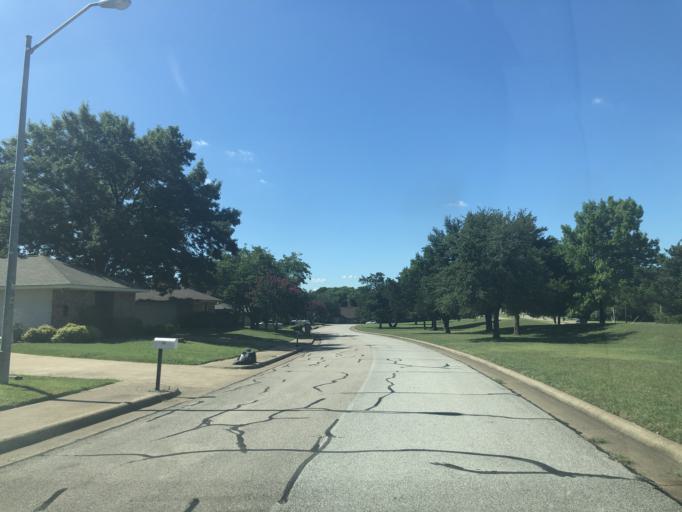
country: US
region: Texas
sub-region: Dallas County
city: Duncanville
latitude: 32.6437
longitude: -96.9421
